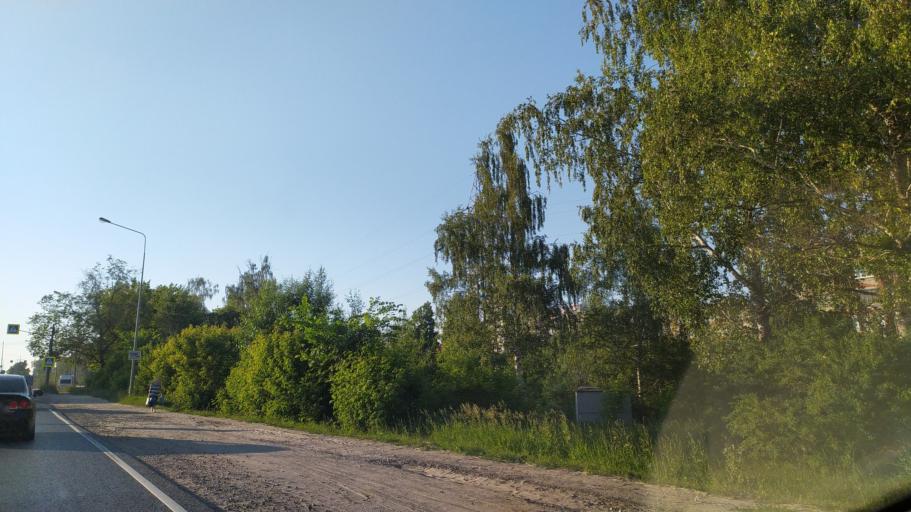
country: RU
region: Chuvashia
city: Kugesi
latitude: 56.0739
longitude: 47.2776
